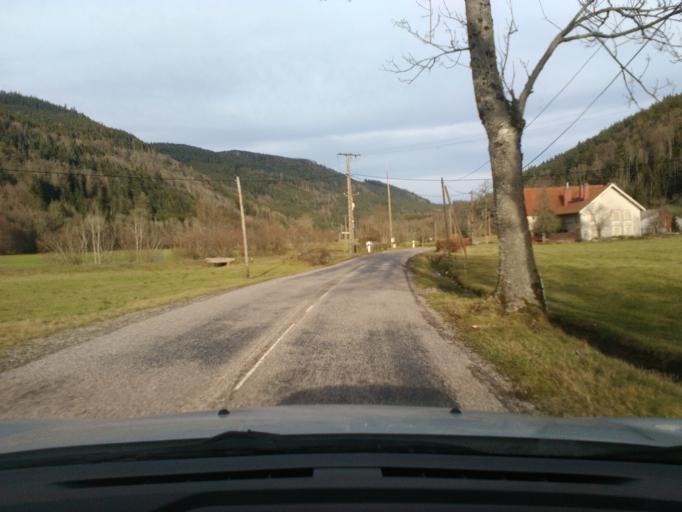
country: FR
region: Lorraine
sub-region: Departement des Vosges
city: Xonrupt-Longemer
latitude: 48.1239
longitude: 6.9533
